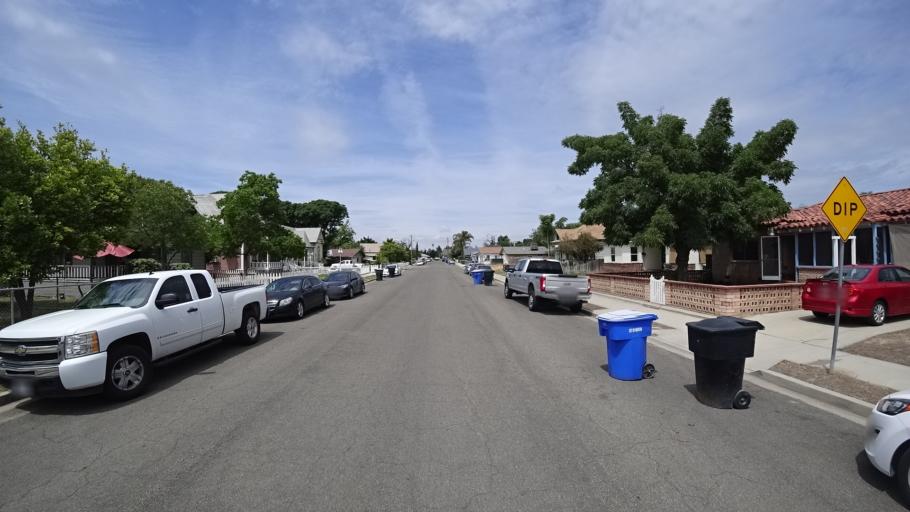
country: US
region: California
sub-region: Kings County
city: Hanford
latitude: 36.3292
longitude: -119.6401
